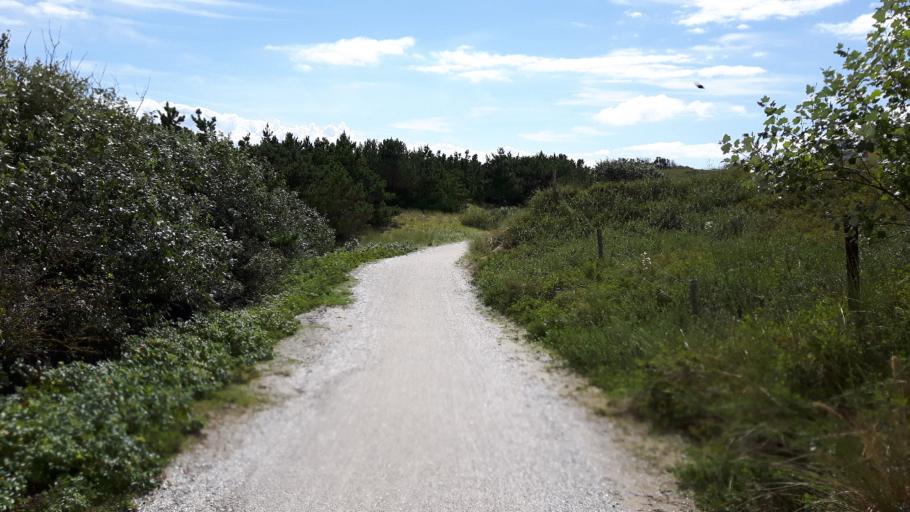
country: NL
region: Friesland
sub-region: Gemeente Ameland
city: Hollum
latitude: 53.4475
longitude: 5.6175
